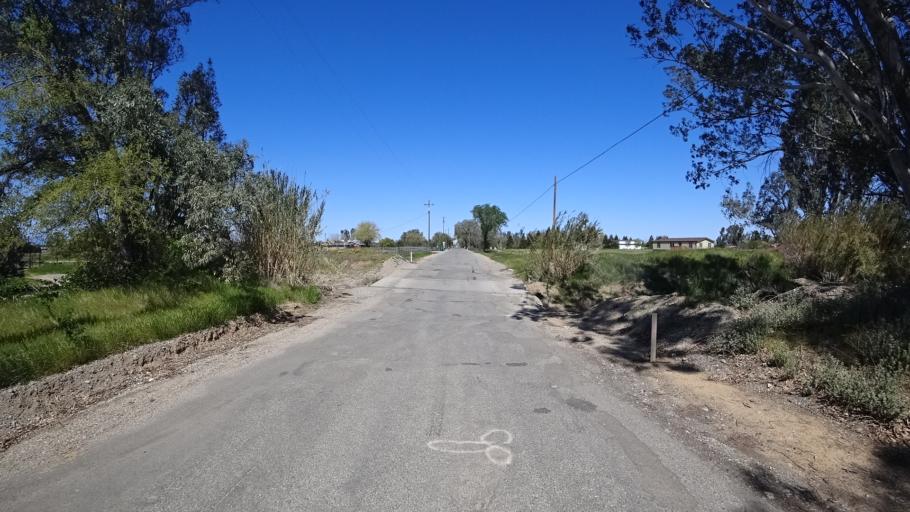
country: US
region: California
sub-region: Glenn County
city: Orland
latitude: 39.7663
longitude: -122.2297
